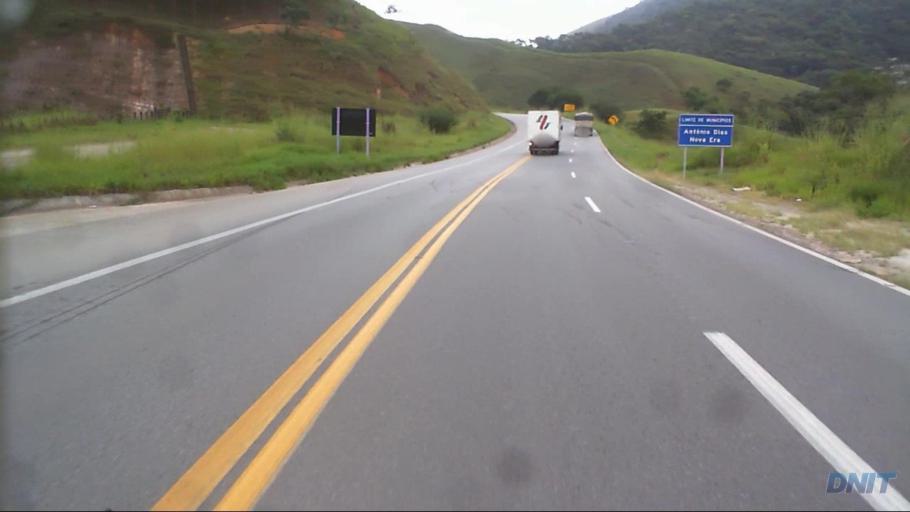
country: BR
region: Minas Gerais
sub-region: Nova Era
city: Nova Era
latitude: -19.6690
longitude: -42.9676
